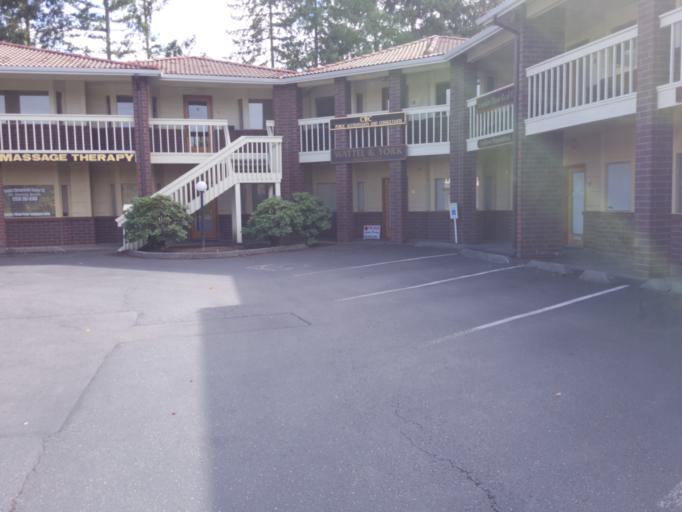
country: US
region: Washington
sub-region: Pierce County
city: Fircrest
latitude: 47.2425
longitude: -122.5217
